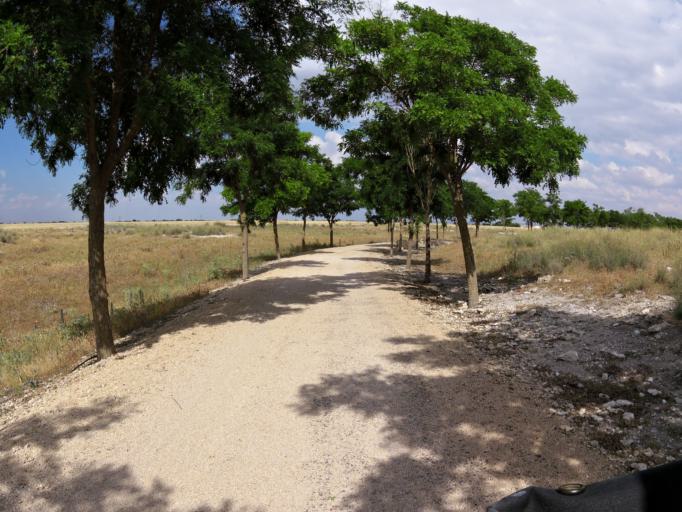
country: ES
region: Castille-La Mancha
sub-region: Provincia de Albacete
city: Albacete
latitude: 38.9661
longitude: -1.9500
